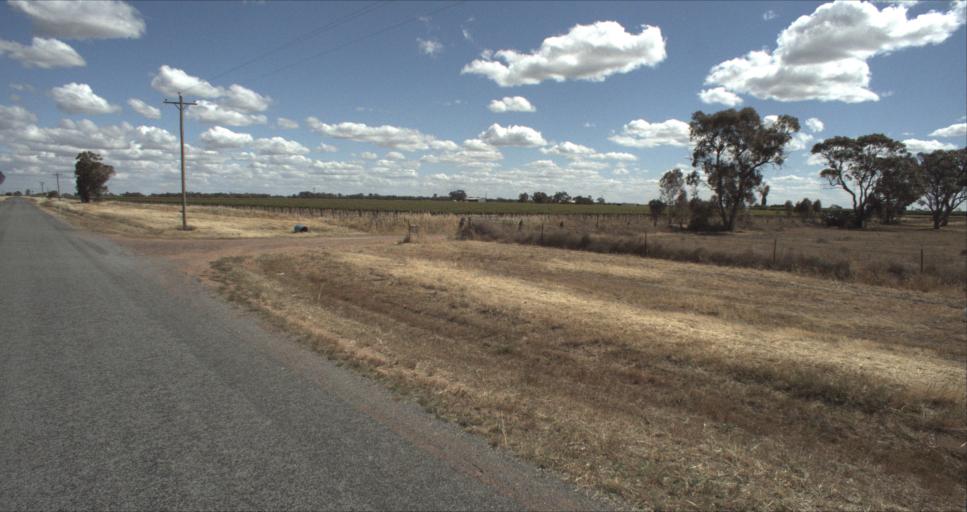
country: AU
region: New South Wales
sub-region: Leeton
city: Leeton
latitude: -34.4919
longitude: 146.2471
